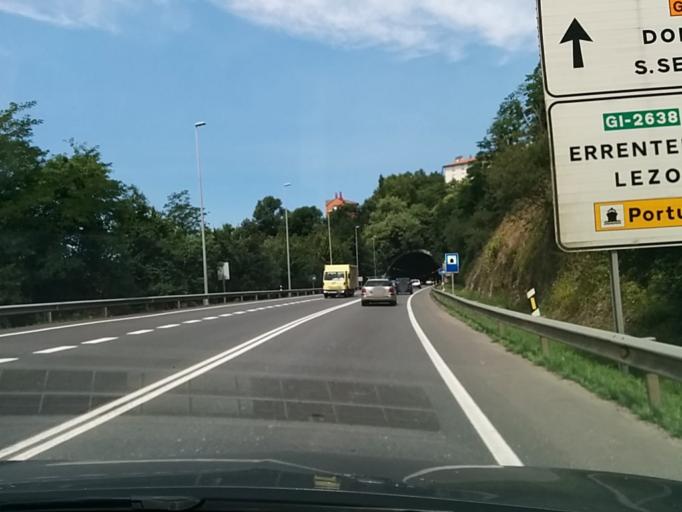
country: ES
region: Basque Country
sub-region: Provincia de Guipuzcoa
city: Lezo
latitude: 43.3150
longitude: -1.8964
